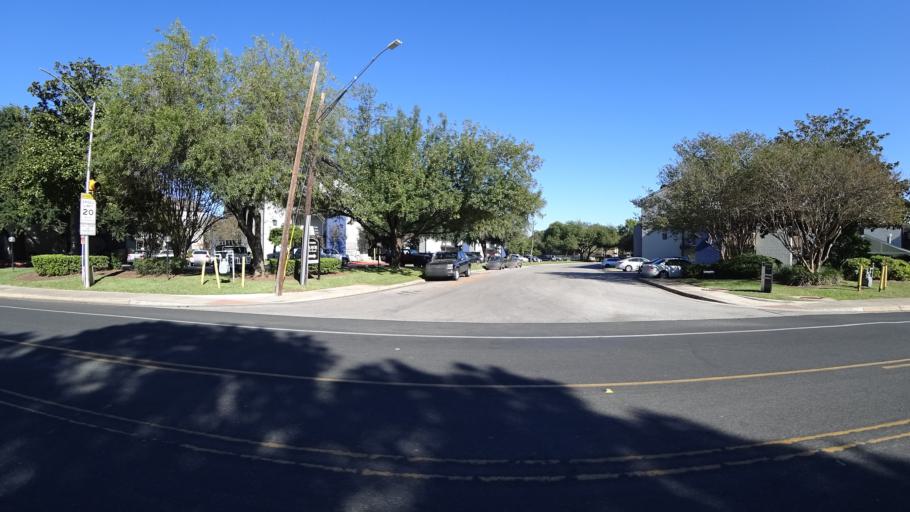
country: US
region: Texas
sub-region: Travis County
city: Rollingwood
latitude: 30.2343
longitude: -97.7901
